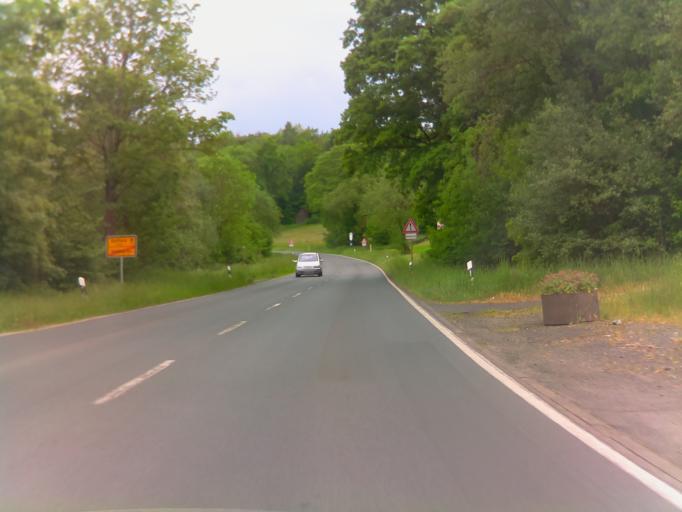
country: DE
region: Hesse
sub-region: Regierungsbezirk Giessen
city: Homberg
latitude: 50.7200
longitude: 9.0060
